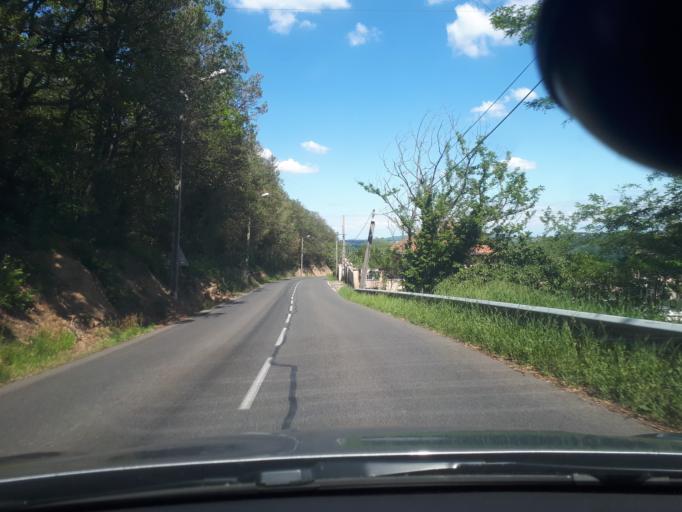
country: FR
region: Rhone-Alpes
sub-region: Departement du Rhone
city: Chassagny
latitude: 45.5844
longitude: 4.7434
